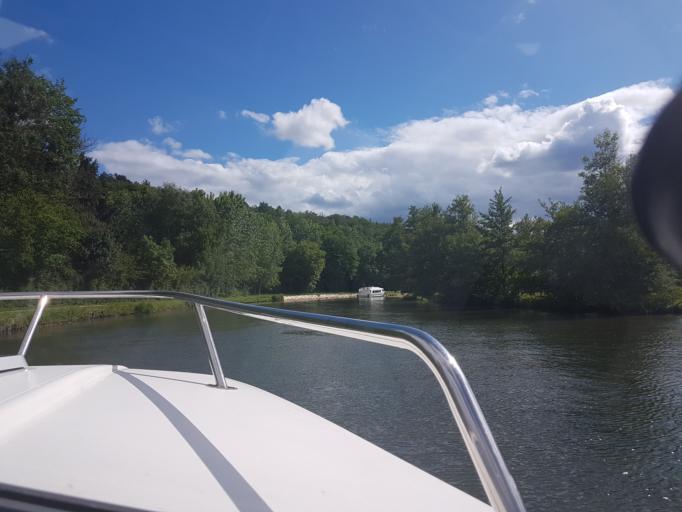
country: FR
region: Bourgogne
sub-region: Departement de l'Yonne
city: Vermenton
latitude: 47.5610
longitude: 3.6507
